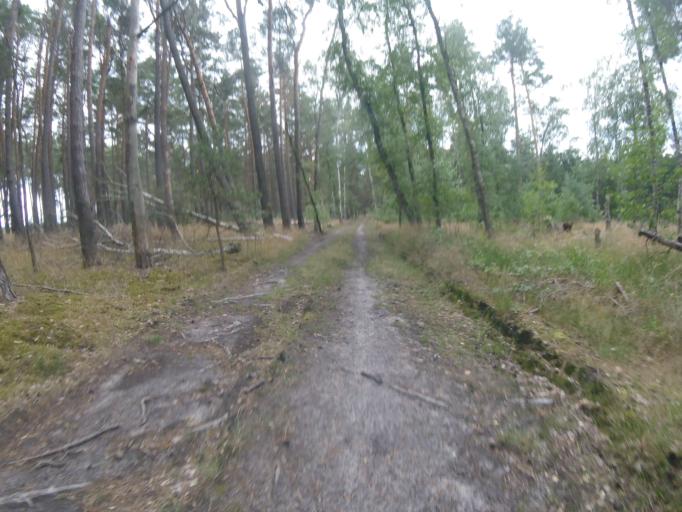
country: DE
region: Brandenburg
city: Bestensee
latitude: 52.2703
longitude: 13.7143
